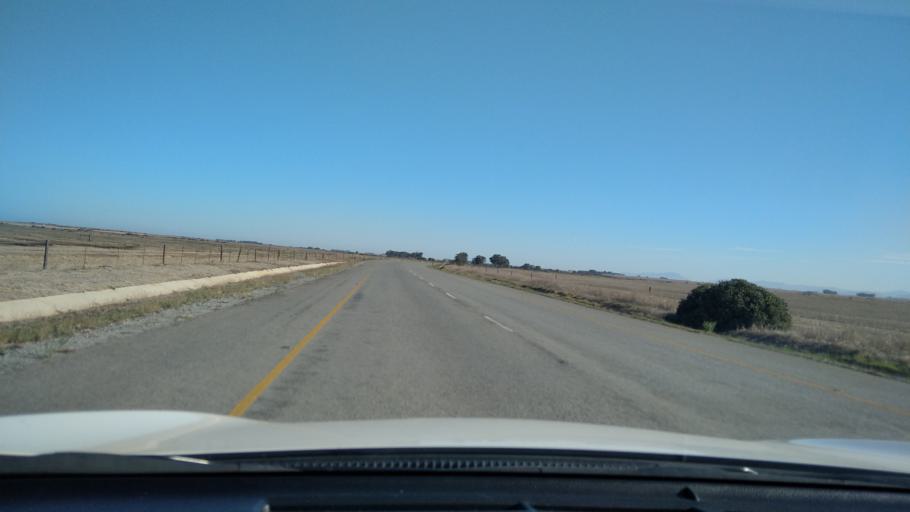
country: ZA
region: Western Cape
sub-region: West Coast District Municipality
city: Moorreesburg
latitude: -33.2833
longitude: 18.6045
